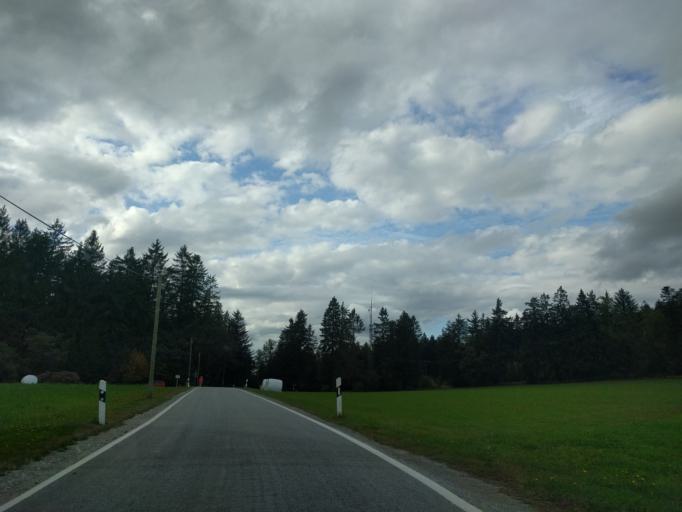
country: DE
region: Bavaria
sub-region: Lower Bavaria
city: Schaufling
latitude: 48.8742
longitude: 13.0249
